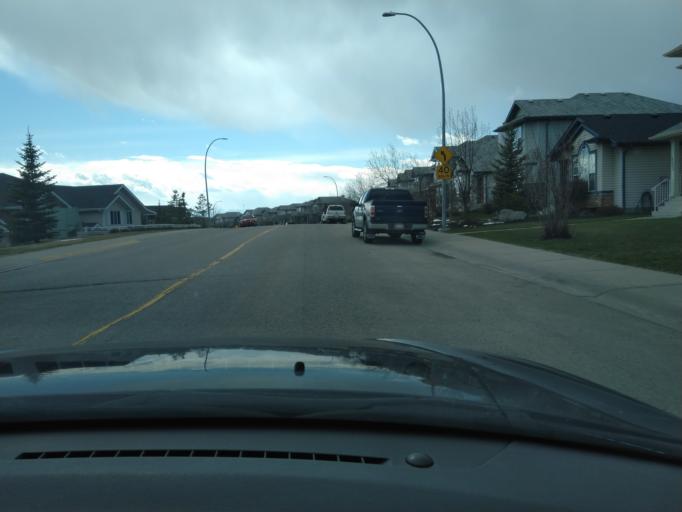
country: CA
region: Alberta
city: Calgary
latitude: 51.1337
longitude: -114.2157
